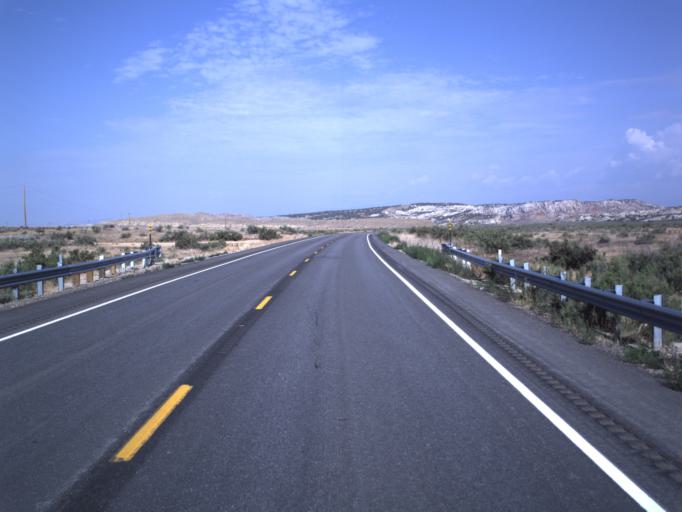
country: US
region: Utah
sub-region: Uintah County
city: Naples
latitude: 40.3081
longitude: -109.2155
